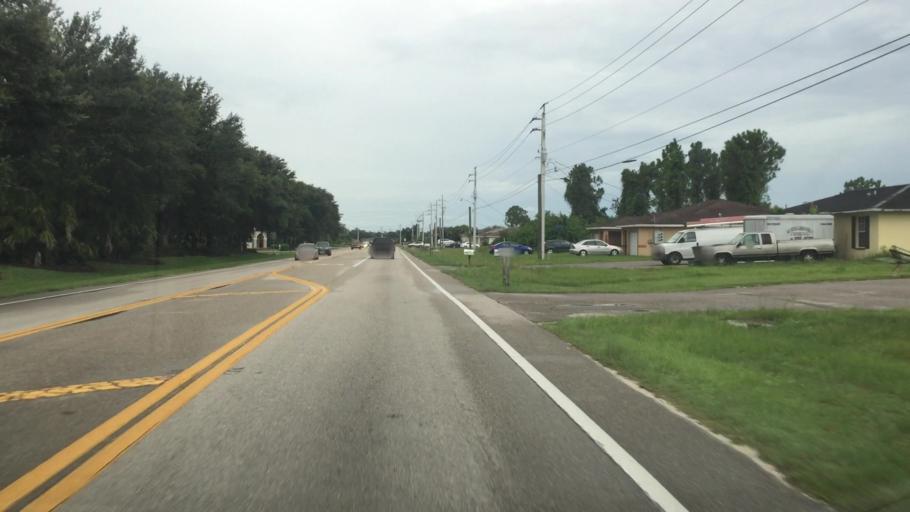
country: US
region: Florida
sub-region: Lee County
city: Gateway
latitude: 26.6016
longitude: -81.7360
